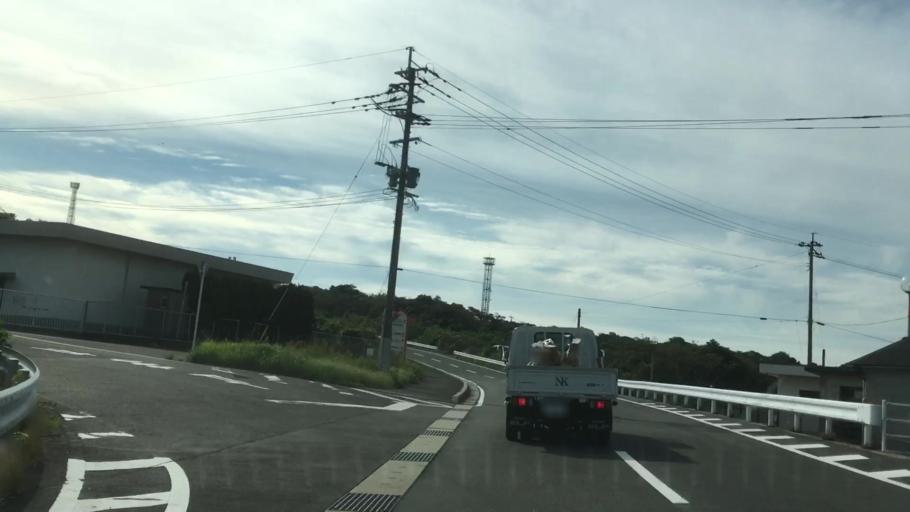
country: JP
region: Nagasaki
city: Sasebo
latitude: 33.0219
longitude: 129.5724
